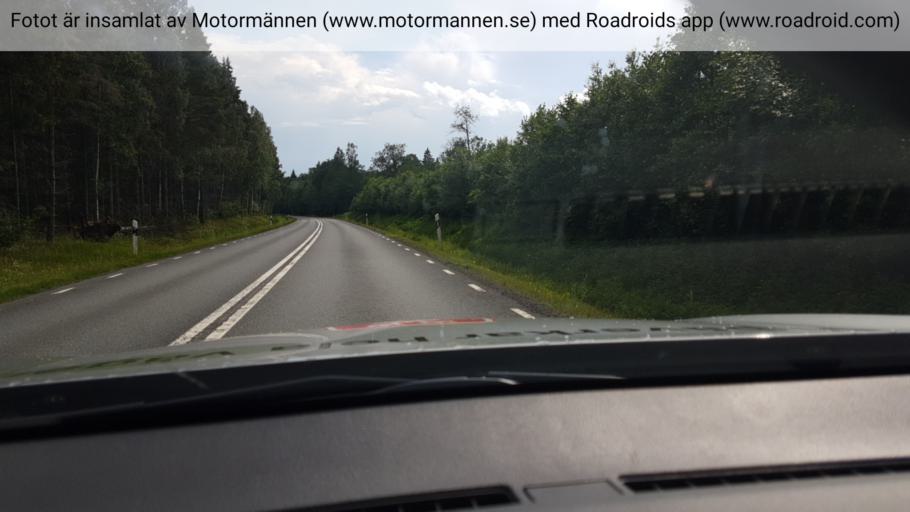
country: SE
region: Vaestra Goetaland
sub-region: Hjo Kommun
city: Hjo
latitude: 58.1133
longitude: 14.2093
